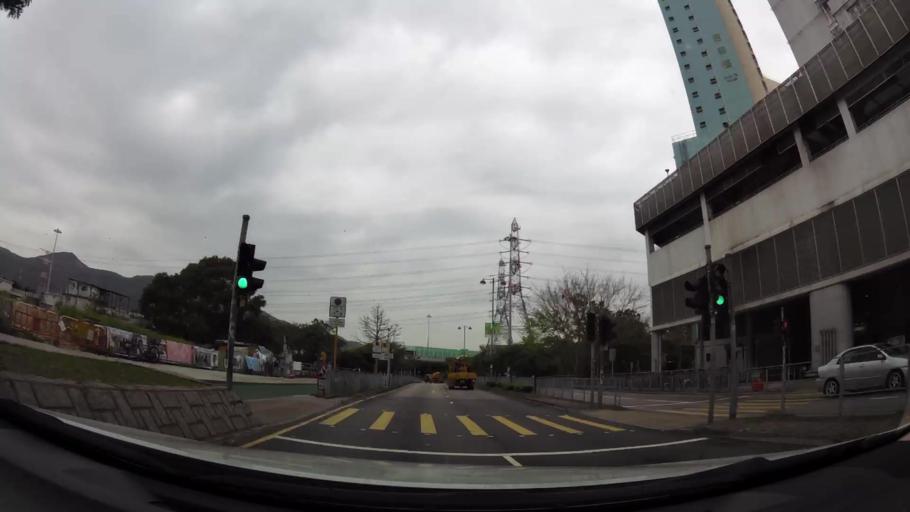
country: HK
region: Tuen Mun
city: Tuen Mun
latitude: 22.4135
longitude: 113.9823
